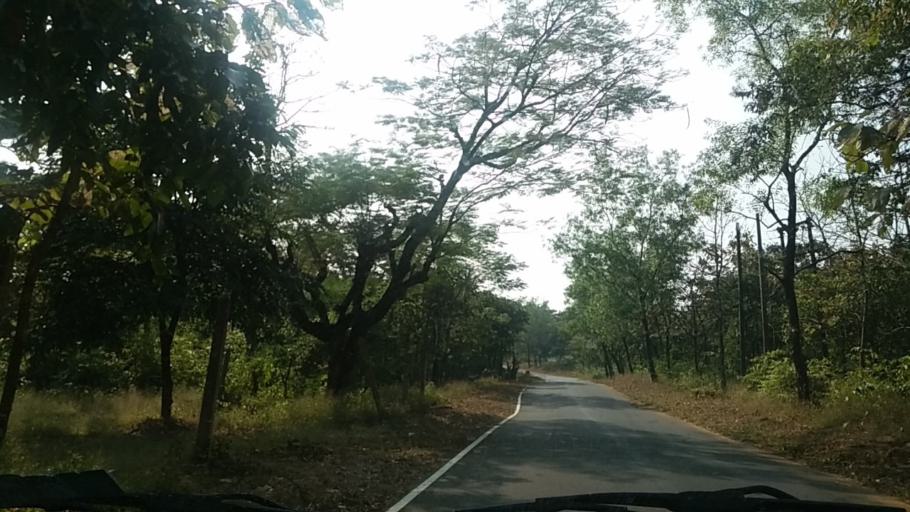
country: IN
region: Goa
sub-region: South Goa
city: Sanguem
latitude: 15.1973
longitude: 74.2272
